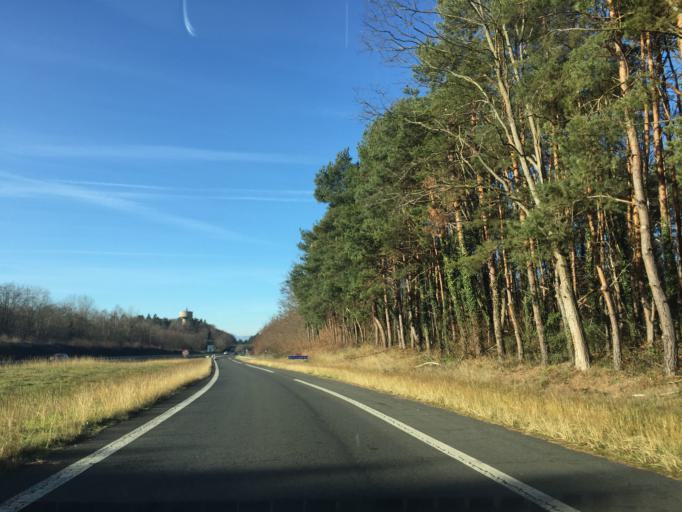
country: FR
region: Auvergne
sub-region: Departement du Puy-de-Dome
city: Orleat
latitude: 45.8522
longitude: 3.4012
